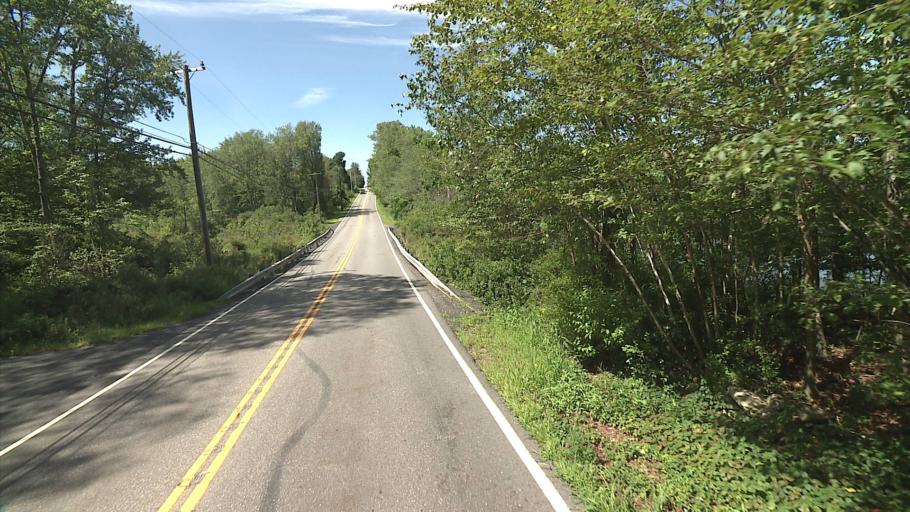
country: US
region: Connecticut
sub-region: Windham County
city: South Woodstock
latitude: 41.8951
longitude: -72.0563
